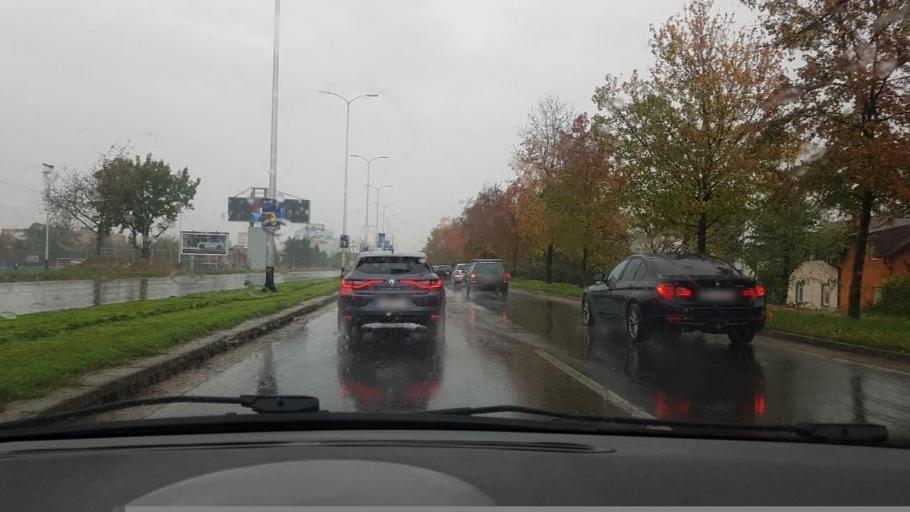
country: HR
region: Grad Zagreb
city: Novi Zagreb
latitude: 45.7947
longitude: 15.9841
